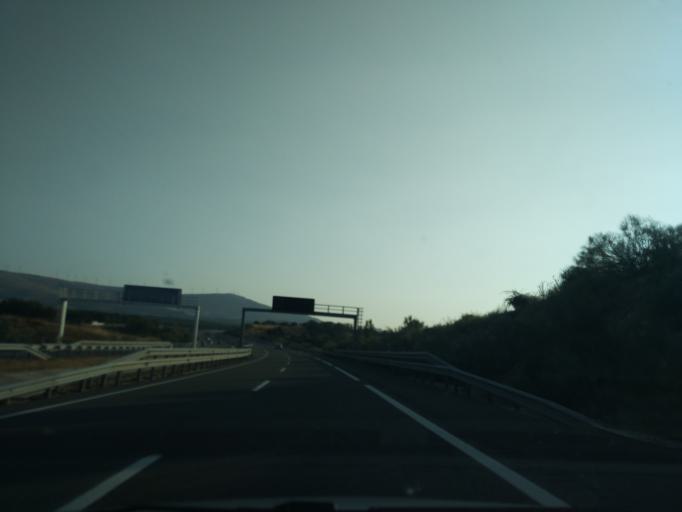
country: ES
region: Castille and Leon
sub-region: Provincia de Segovia
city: Villacastin
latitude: 40.7660
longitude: -4.4374
